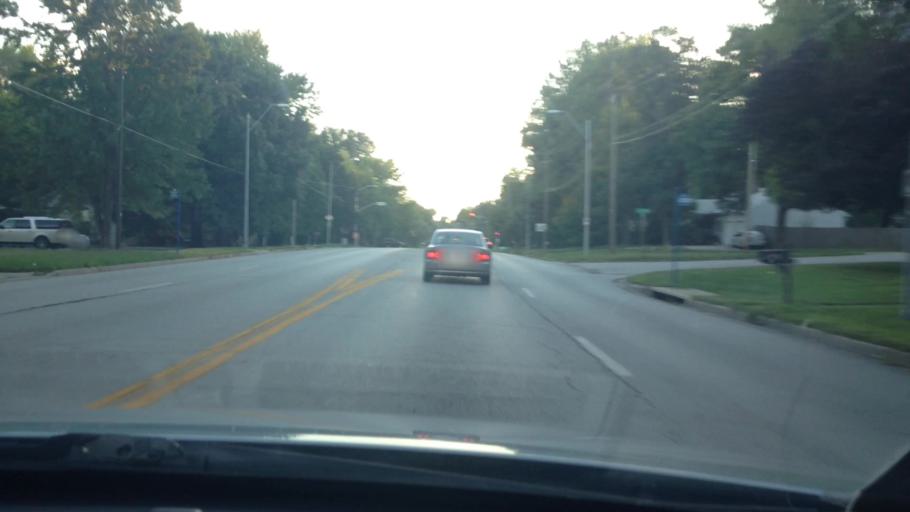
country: US
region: Missouri
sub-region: Jackson County
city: Raytown
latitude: 38.9818
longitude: -94.4847
